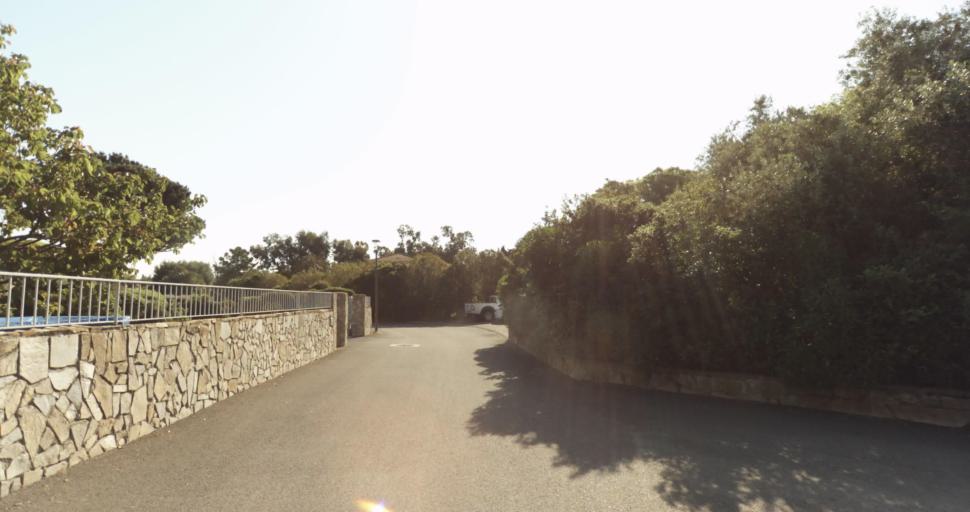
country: FR
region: Corsica
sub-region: Departement de la Haute-Corse
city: Biguglia
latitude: 42.6340
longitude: 9.4333
